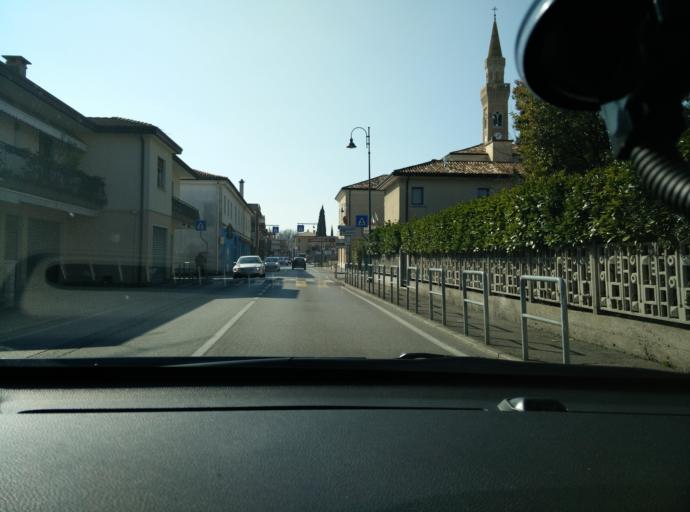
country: IT
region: Veneto
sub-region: Provincia di Venezia
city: Noventa di Piave
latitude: 45.6630
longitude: 12.5309
